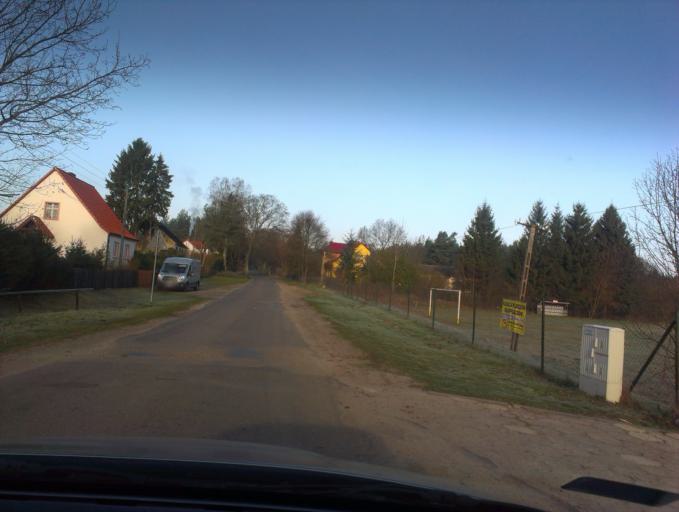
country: PL
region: West Pomeranian Voivodeship
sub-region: Powiat szczecinecki
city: Szczecinek
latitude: 53.8014
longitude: 16.6855
